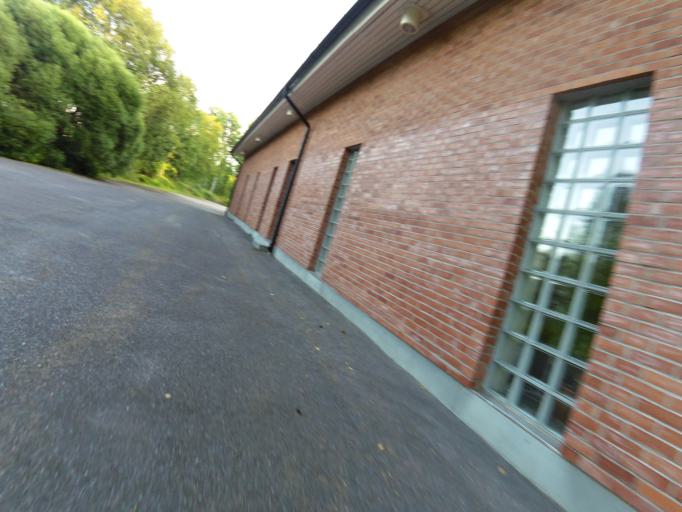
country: SE
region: Gaevleborg
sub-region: Gavle Kommun
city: Gavle
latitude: 60.6552
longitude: 17.1538
